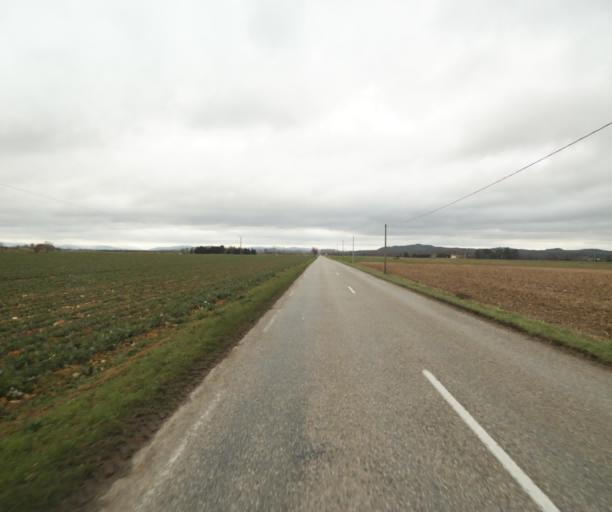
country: FR
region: Midi-Pyrenees
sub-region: Departement de l'Ariege
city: Saverdun
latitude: 43.2088
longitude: 1.6277
